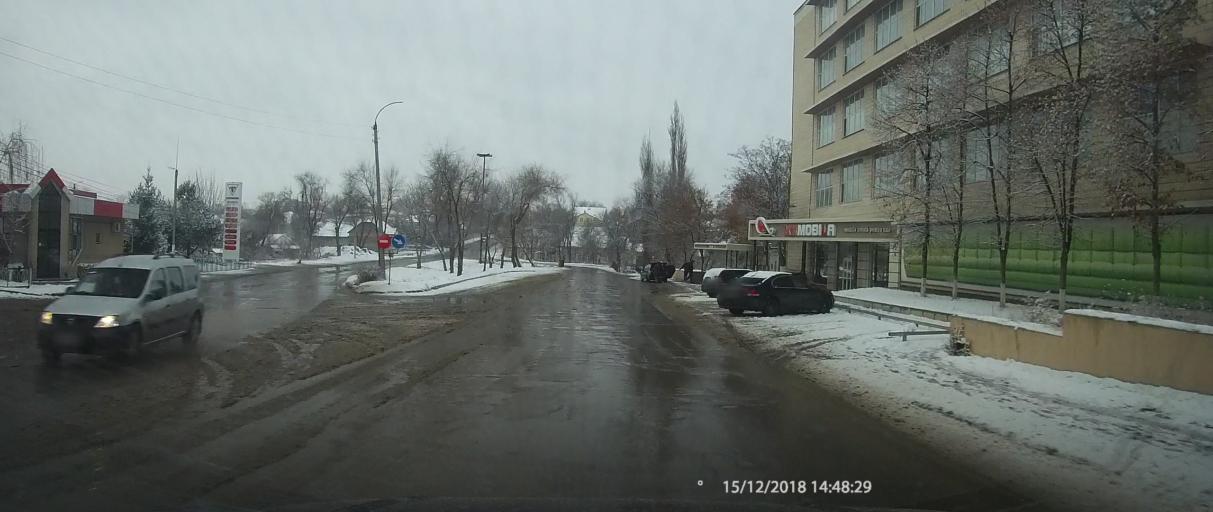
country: MD
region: Cahul
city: Cahul
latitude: 45.8977
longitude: 28.1978
